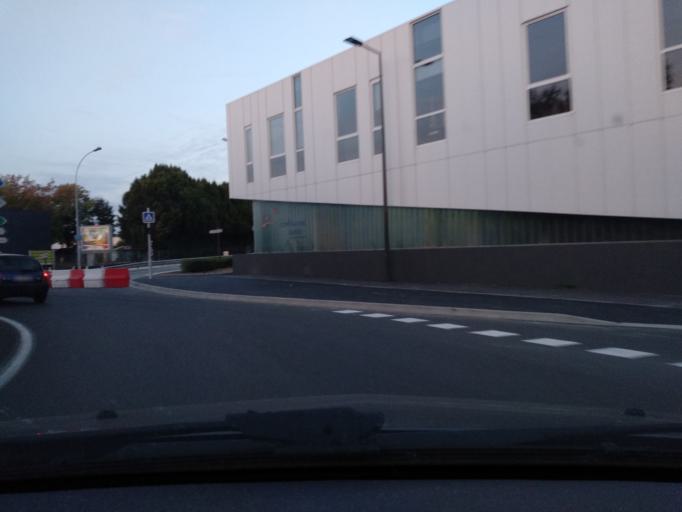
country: FR
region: Centre
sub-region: Departement d'Indre-et-Loire
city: Saint-Cyr-sur-Loire
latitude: 47.4297
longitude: 0.6789
